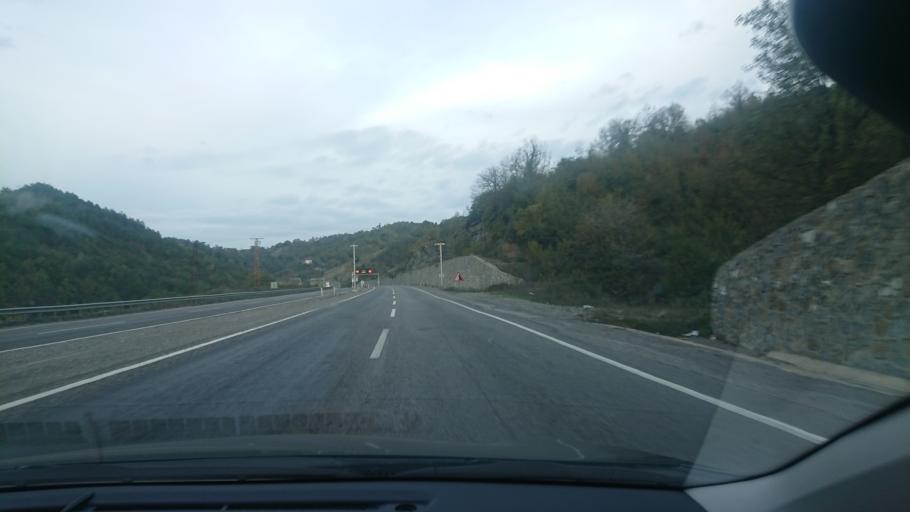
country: TR
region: Zonguldak
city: Beycuma
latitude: 41.4084
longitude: 31.9328
